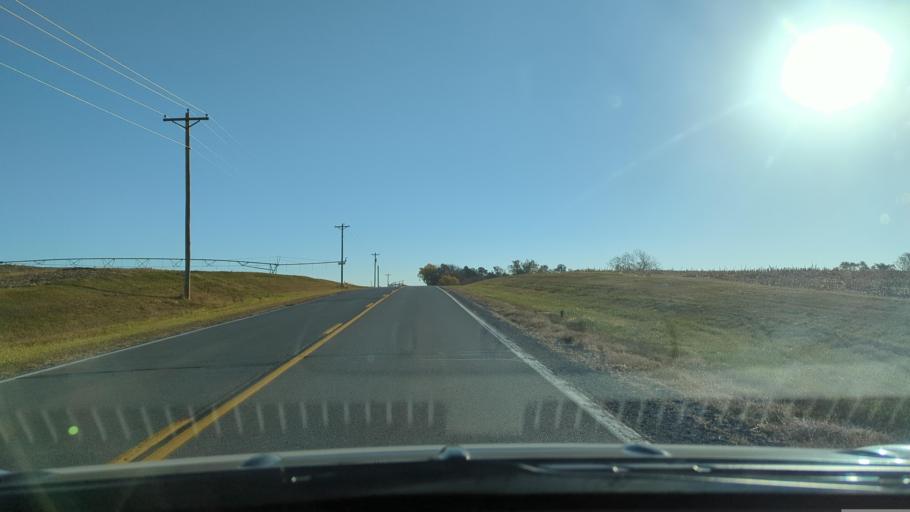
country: US
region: Nebraska
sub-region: Sarpy County
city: Springfield
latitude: 41.0890
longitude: -96.1646
